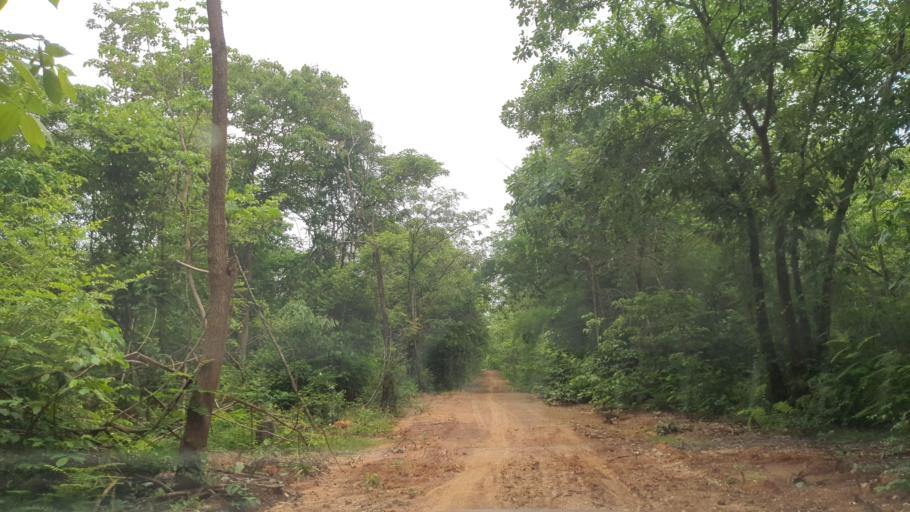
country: TH
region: Sukhothai
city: Thung Saliam
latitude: 17.2397
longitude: 99.5434
